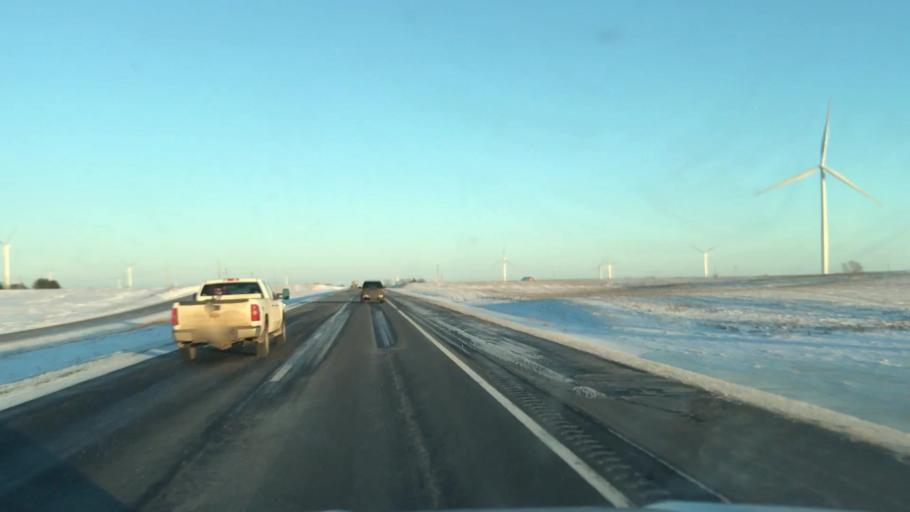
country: US
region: Missouri
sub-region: DeKalb County
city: Maysville
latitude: 39.7617
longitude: -94.4382
